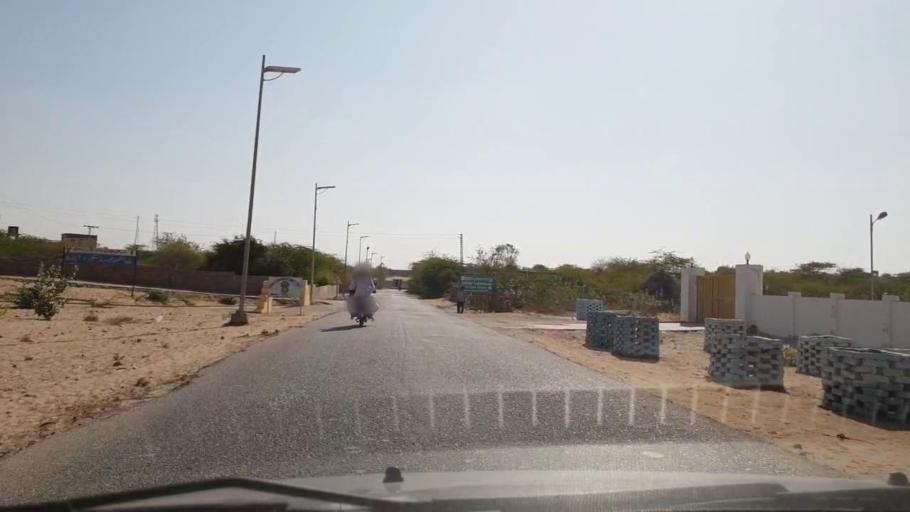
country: PK
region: Sindh
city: Diplo
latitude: 24.4757
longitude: 69.5807
